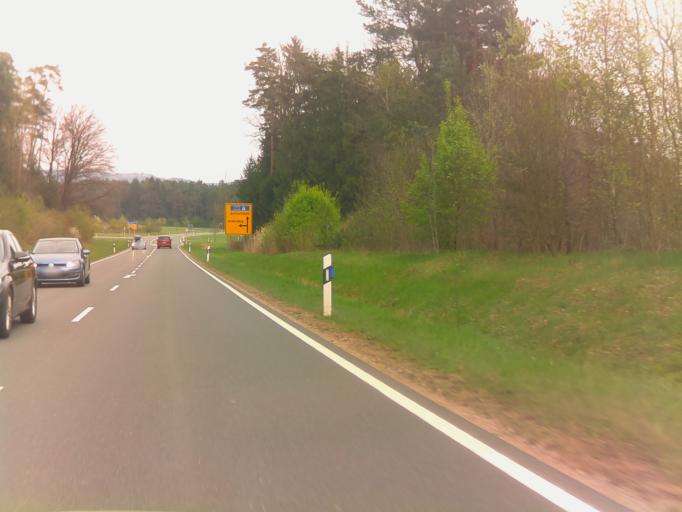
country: DE
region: Bavaria
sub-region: Regierungsbezirk Mittelfranken
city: Simmelsdorf
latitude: 49.5744
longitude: 11.2922
